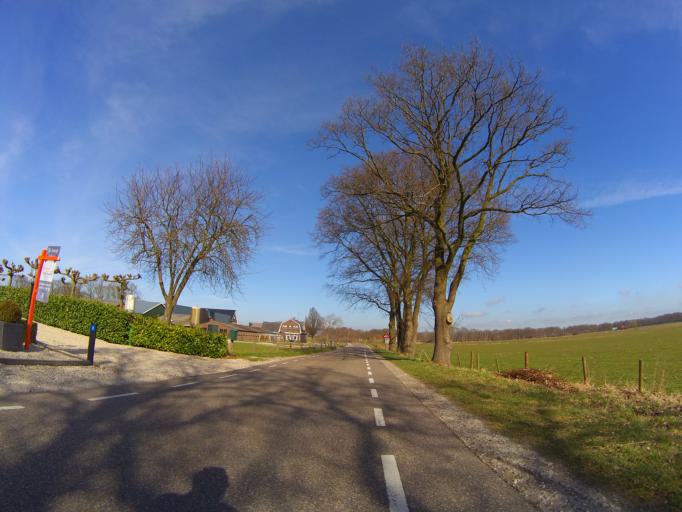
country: NL
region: Utrecht
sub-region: Gemeente Veenendaal
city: Veenendaal
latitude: 52.0464
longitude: 5.5399
